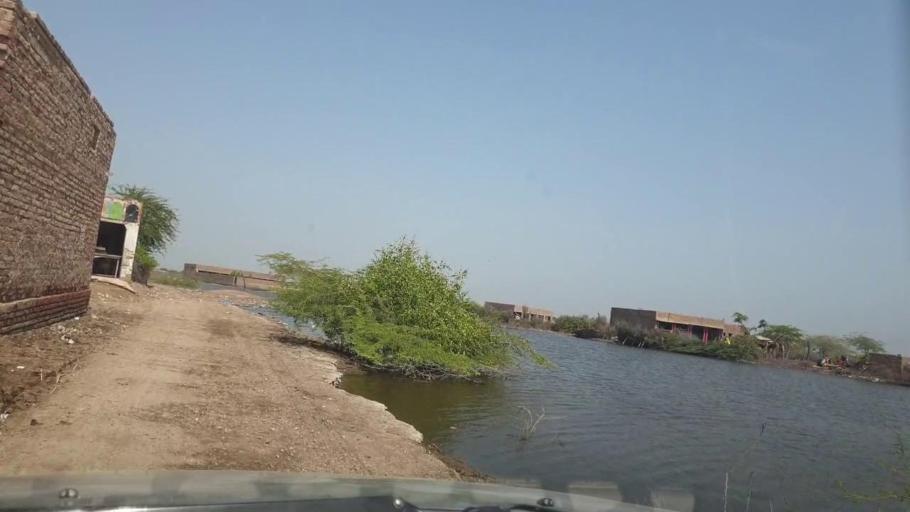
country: PK
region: Sindh
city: Tando Ghulam Ali
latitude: 25.1154
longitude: 68.7864
